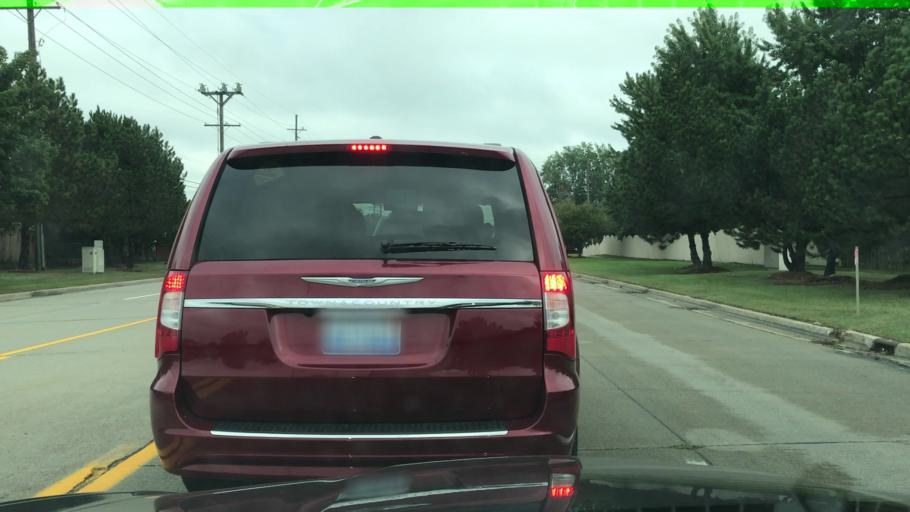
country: US
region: Michigan
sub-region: Macomb County
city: Sterling Heights
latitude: 42.5795
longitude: -83.0568
